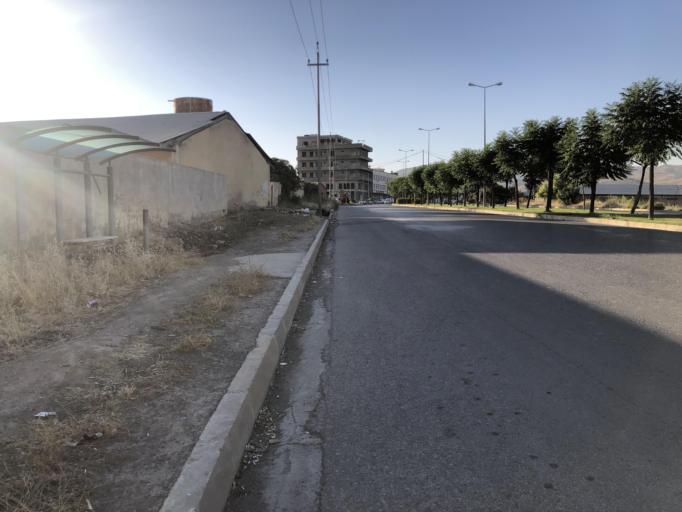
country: IQ
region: Dahuk
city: Dihok
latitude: 36.8575
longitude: 42.9343
